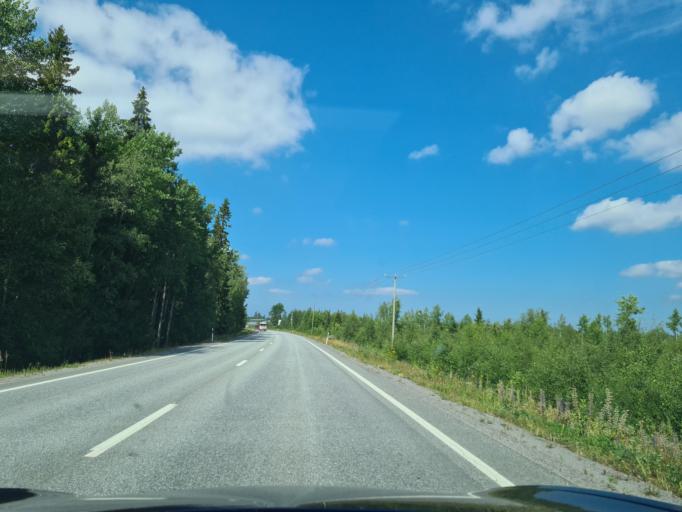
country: FI
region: Ostrobothnia
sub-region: Vaasa
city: Vaasa
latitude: 63.1641
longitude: 21.5905
